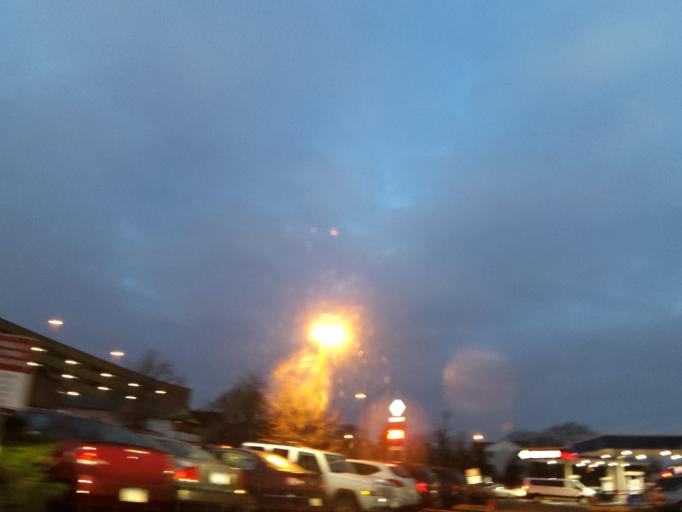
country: US
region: Minnesota
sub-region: Hennepin County
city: Minneapolis
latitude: 44.9650
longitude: -93.2359
